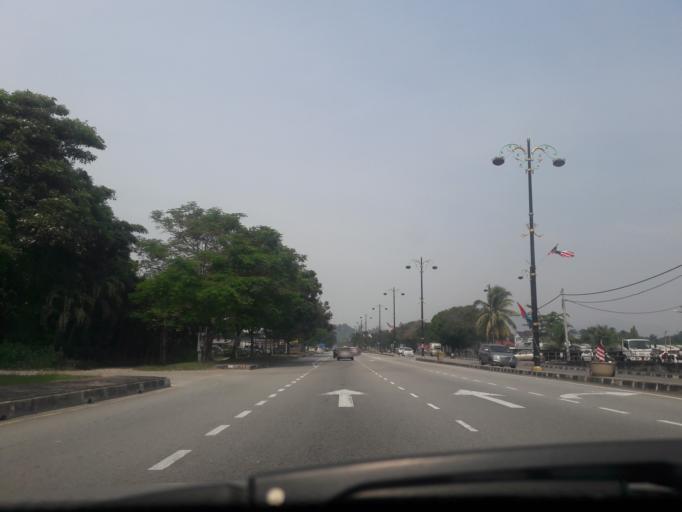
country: MY
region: Kedah
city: Kulim
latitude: 5.3853
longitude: 100.5583
